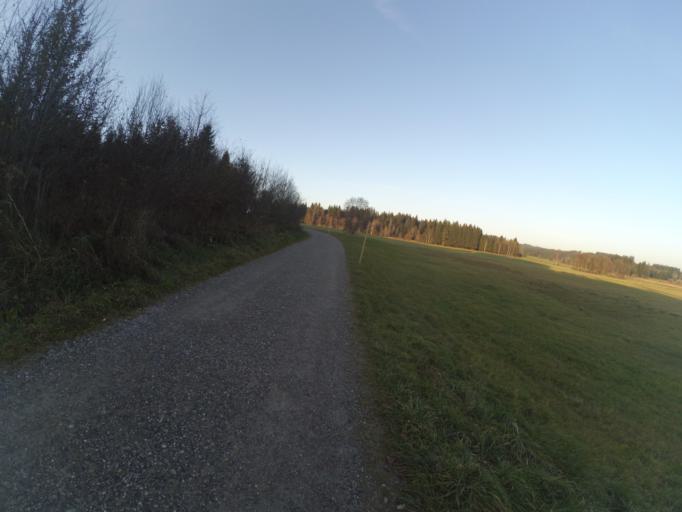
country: DE
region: Bavaria
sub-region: Swabia
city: Aitrang
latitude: 47.8034
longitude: 10.5419
